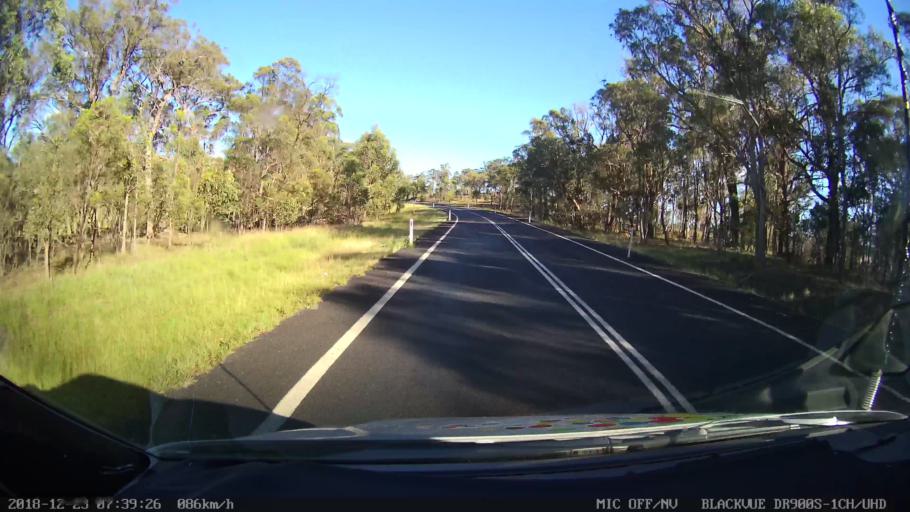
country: AU
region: New South Wales
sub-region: Armidale Dumaresq
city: Enmore
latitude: -30.5169
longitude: 152.0206
